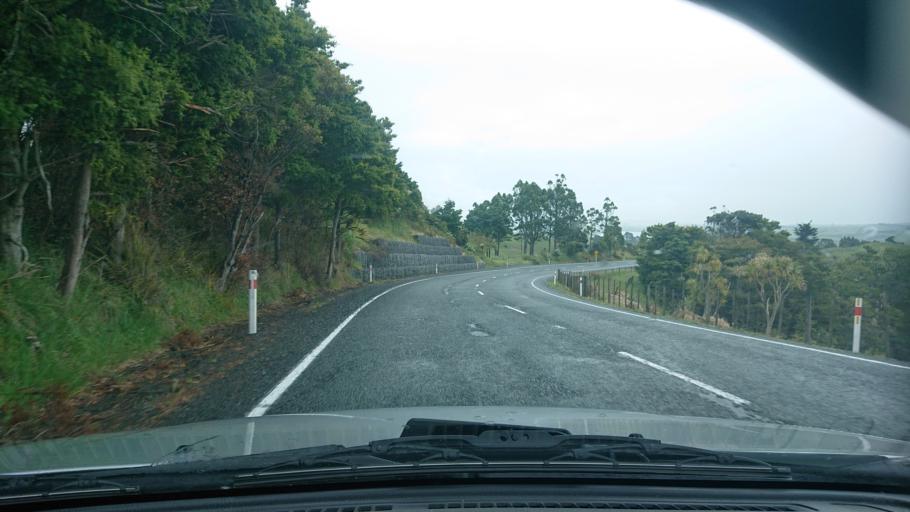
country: NZ
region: Auckland
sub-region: Auckland
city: Wellsford
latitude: -36.3611
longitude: 174.4612
